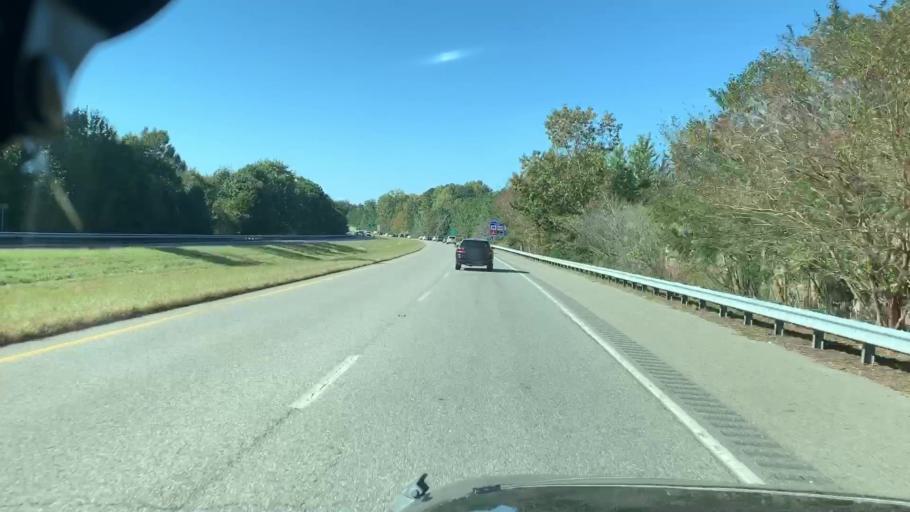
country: US
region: Virginia
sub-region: James City County
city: Williamsburg
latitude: 37.2657
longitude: -76.7429
